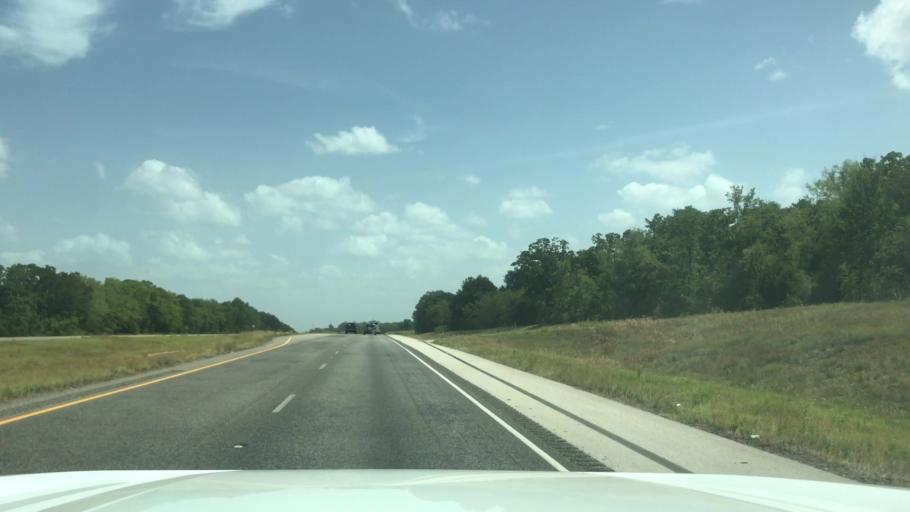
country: US
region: Texas
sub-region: Robertson County
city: Calvert
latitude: 30.9392
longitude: -96.6413
